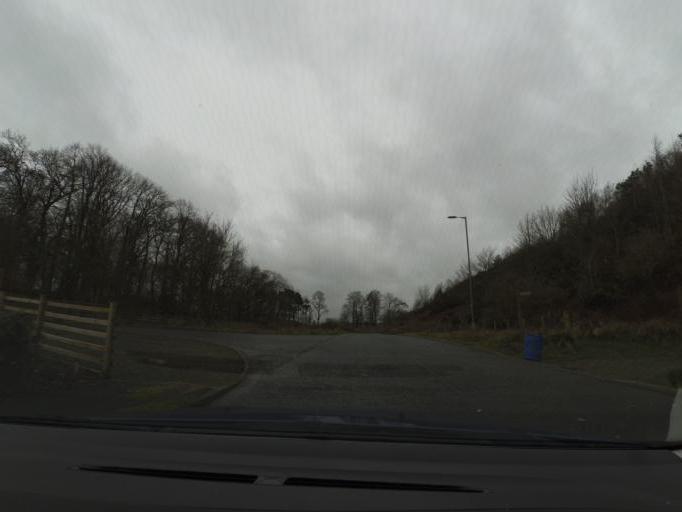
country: GB
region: Scotland
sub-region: The Scottish Borders
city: Hawick
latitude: 55.4397
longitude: -2.7801
